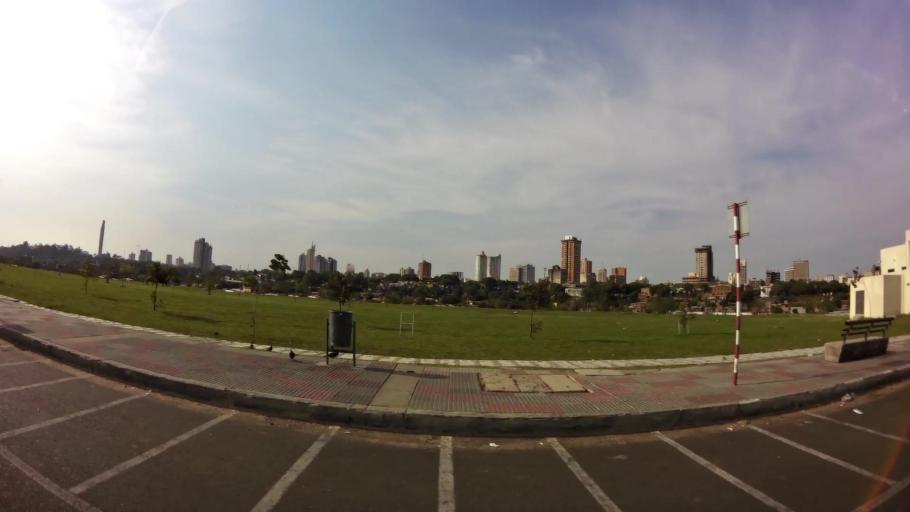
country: PY
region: Asuncion
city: Asuncion
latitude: -25.2773
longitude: -57.6307
